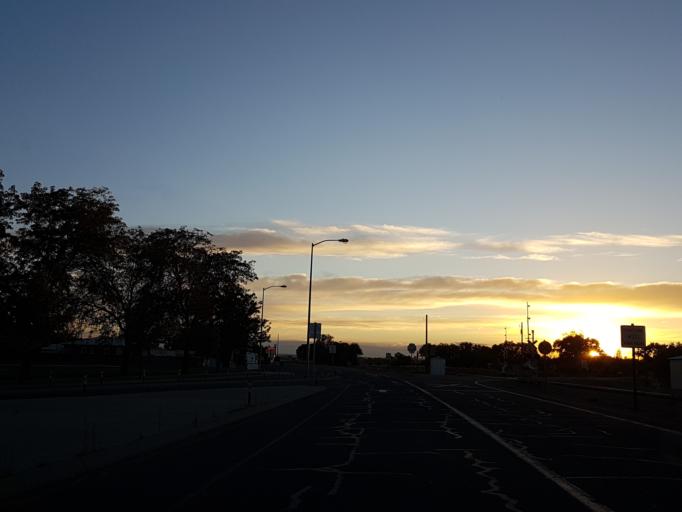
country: US
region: Oregon
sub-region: Malheur County
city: Vale
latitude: 43.9821
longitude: -117.2505
